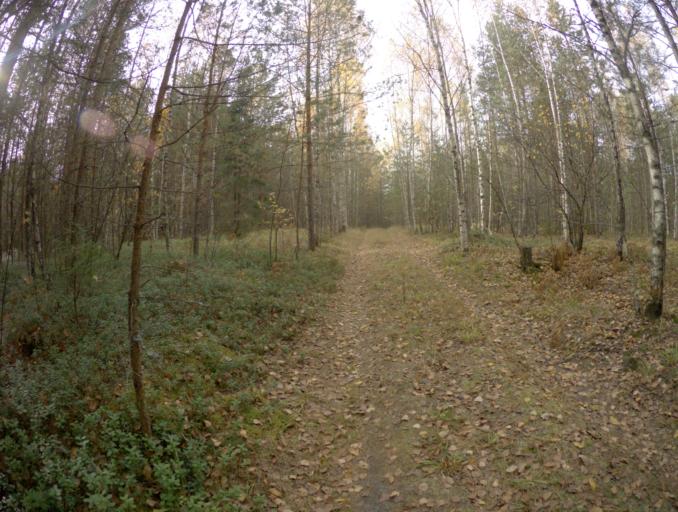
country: RU
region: Vladimir
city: Vorsha
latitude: 55.9661
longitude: 40.1443
